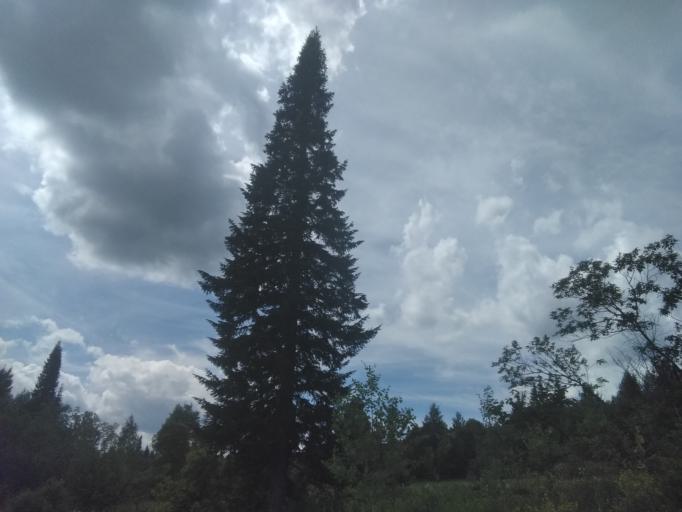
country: RU
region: Chelyabinsk
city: Sim
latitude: 54.9853
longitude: 57.5383
